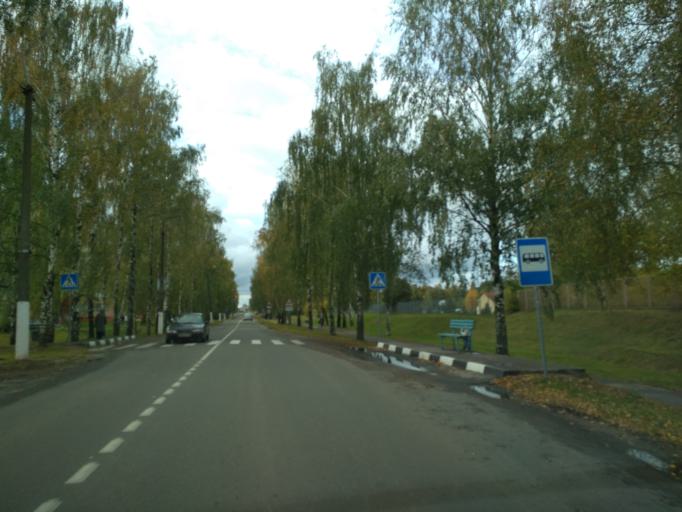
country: BY
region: Minsk
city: Mar''ina Horka
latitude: 53.5049
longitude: 28.1641
